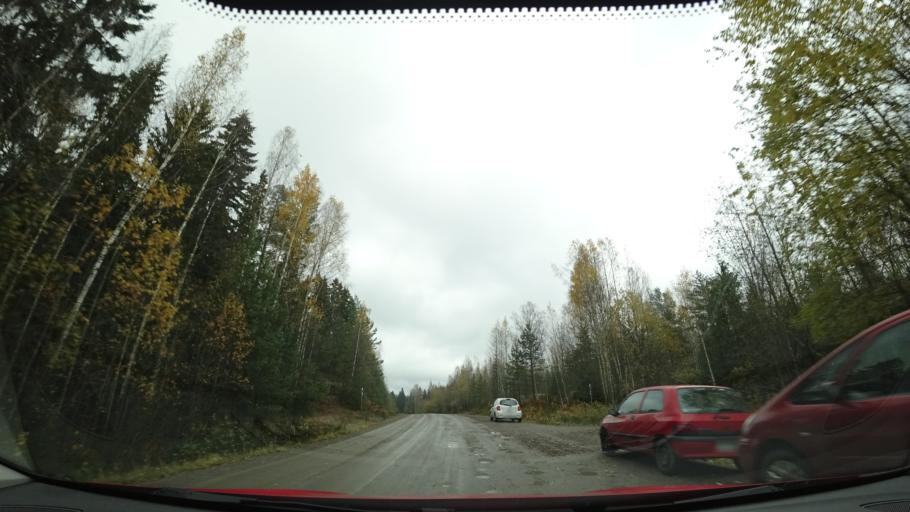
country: FI
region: Uusimaa
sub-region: Helsinki
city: Sibbo
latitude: 60.2922
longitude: 25.1973
